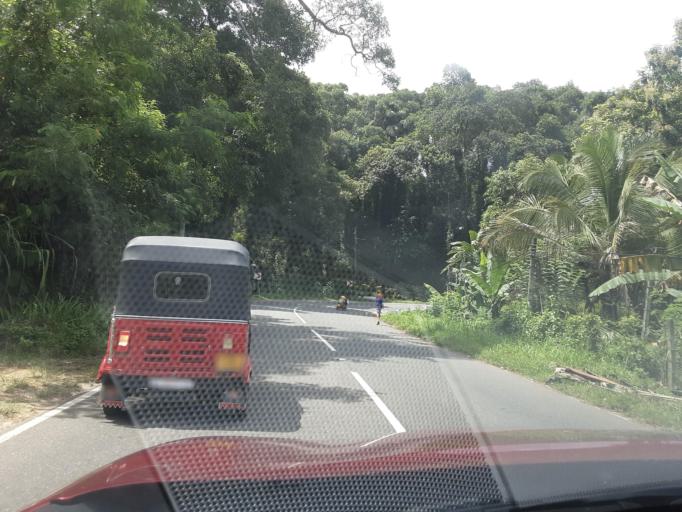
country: LK
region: Uva
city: Monaragala
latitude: 6.8951
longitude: 81.2527
